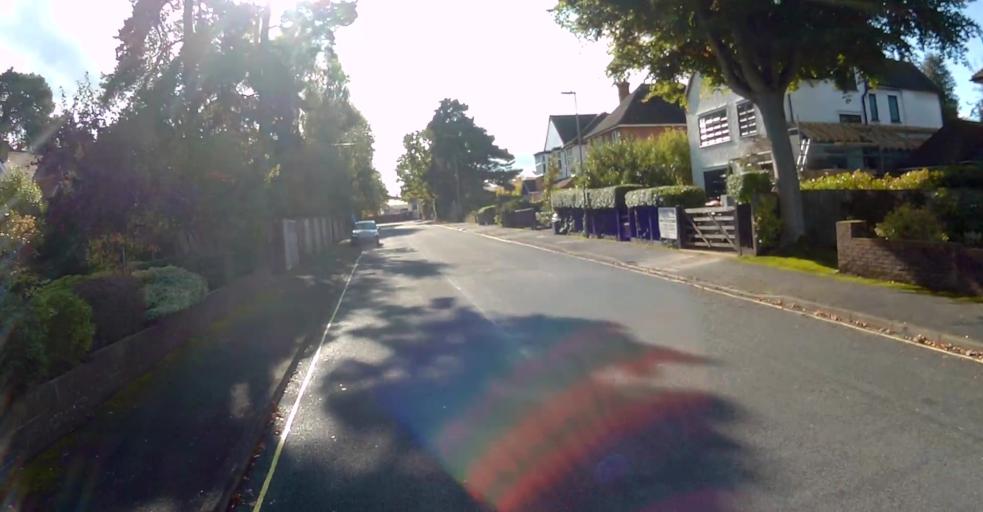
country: GB
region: England
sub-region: Hampshire
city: Farnborough
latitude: 51.2881
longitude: -0.7510
